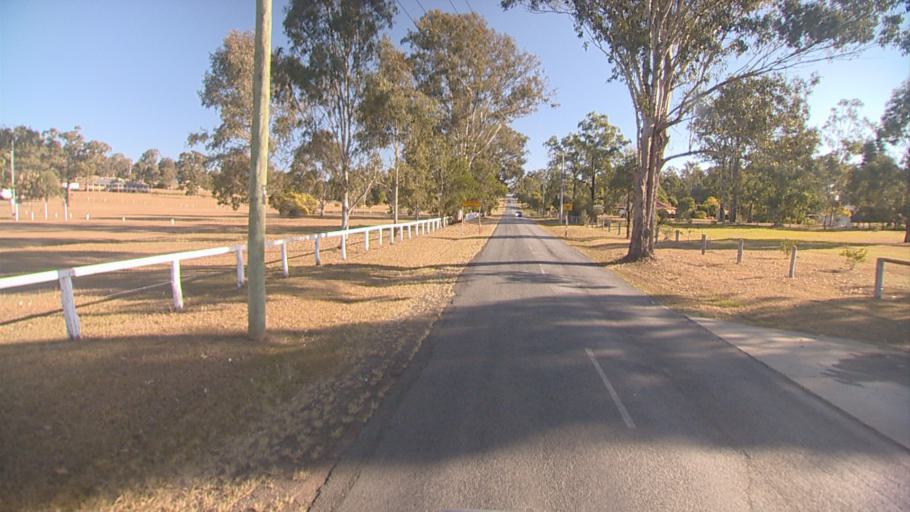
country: AU
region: Queensland
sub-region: Logan
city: Cedar Vale
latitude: -27.8301
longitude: 153.0100
